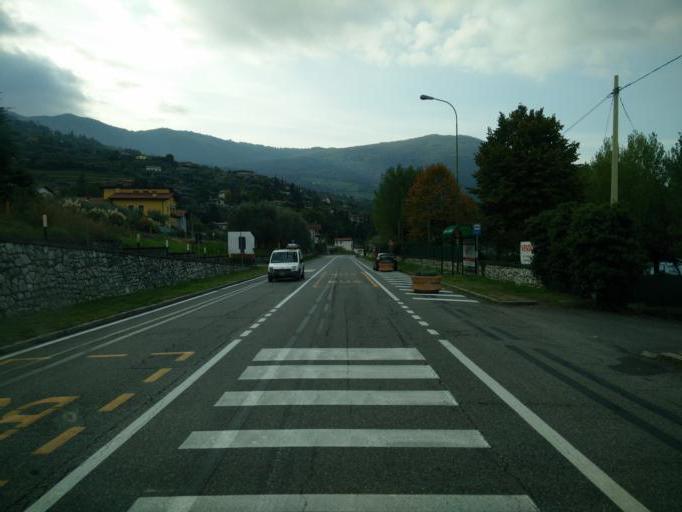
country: IT
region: Lombardy
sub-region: Provincia di Brescia
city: Sale Marasino
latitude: 45.7037
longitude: 10.1083
